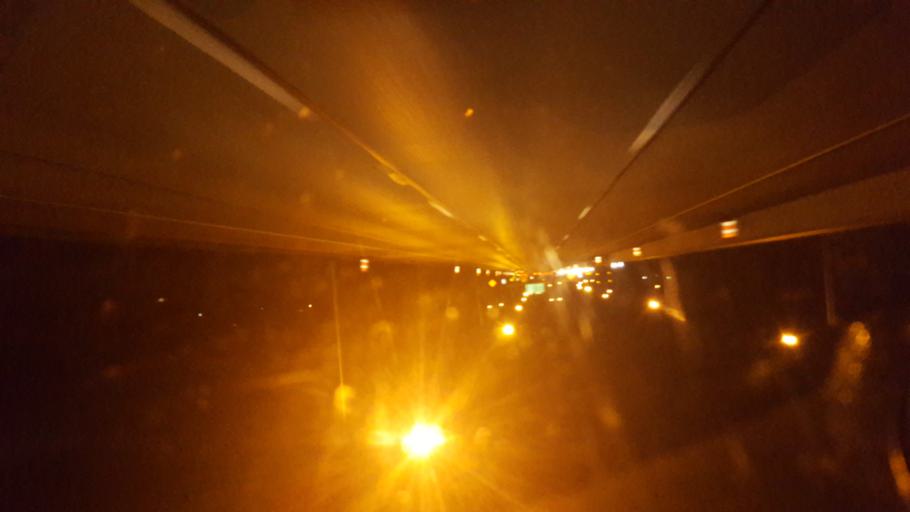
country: US
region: Indiana
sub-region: Marion County
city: Speedway
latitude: 39.7285
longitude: -86.2465
